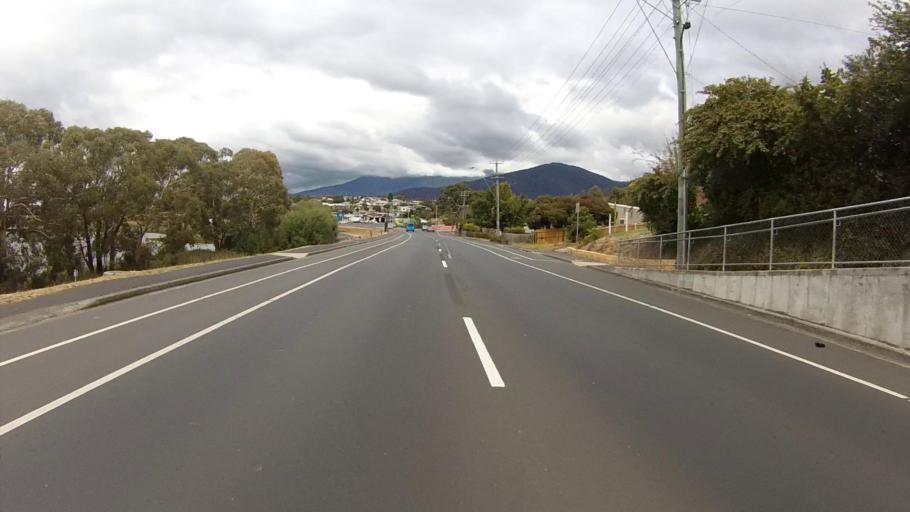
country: AU
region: Tasmania
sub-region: Glenorchy
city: Claremont
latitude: -42.7843
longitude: 147.2522
